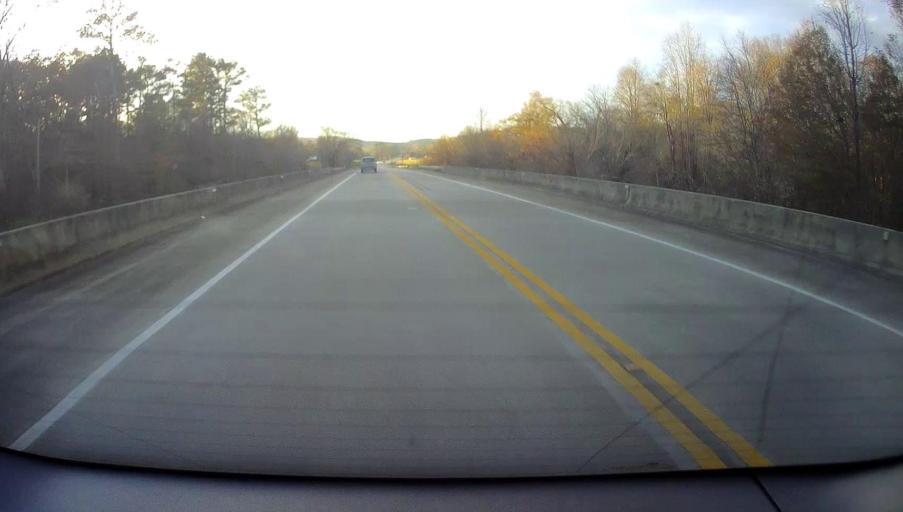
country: US
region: Alabama
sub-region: Saint Clair County
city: Steele
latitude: 34.0660
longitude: -86.2918
